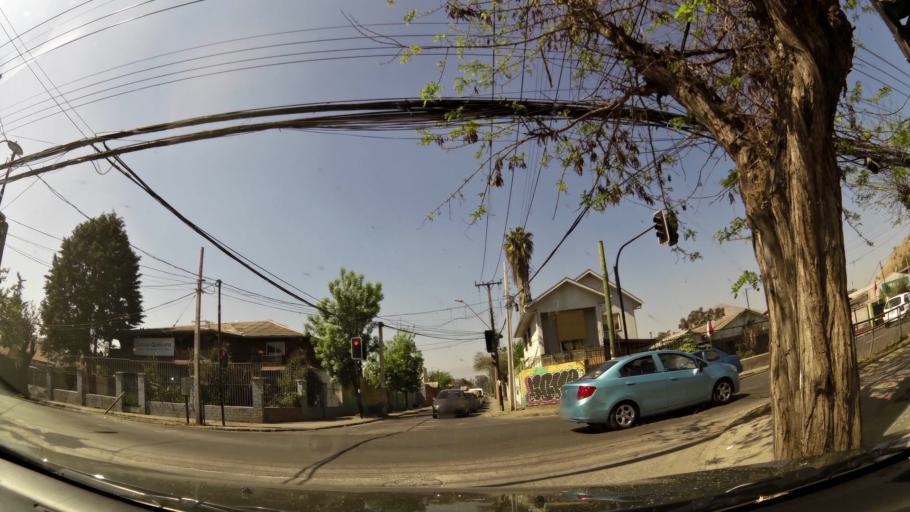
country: CL
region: Santiago Metropolitan
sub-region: Provincia de Santiago
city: Lo Prado
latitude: -33.3687
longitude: -70.7384
